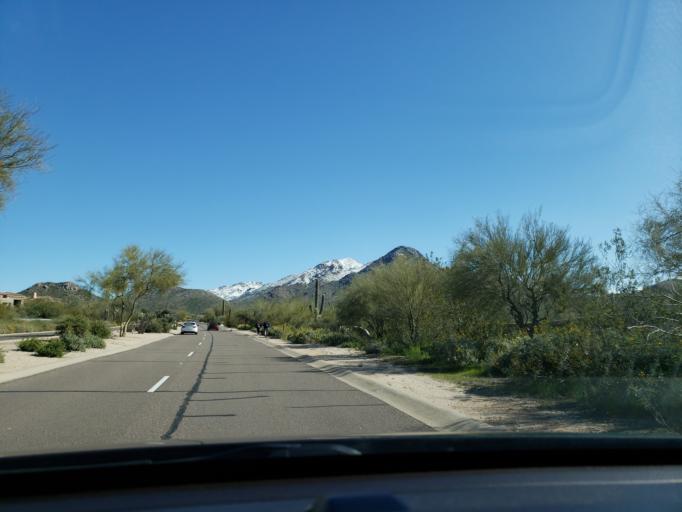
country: US
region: Arizona
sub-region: Maricopa County
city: Carefree
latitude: 33.7079
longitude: -111.8474
